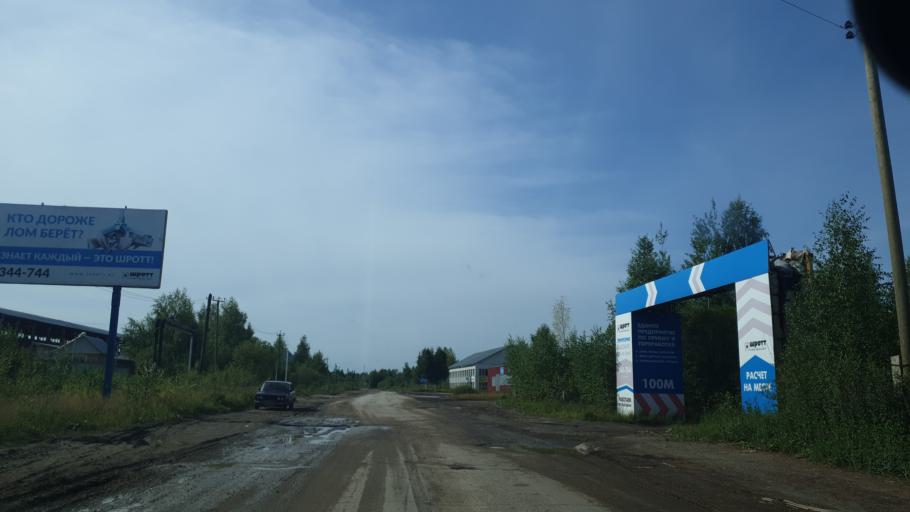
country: RU
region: Komi Republic
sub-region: Syktyvdinskiy Rayon
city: Syktyvkar
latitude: 61.7248
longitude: 50.7510
